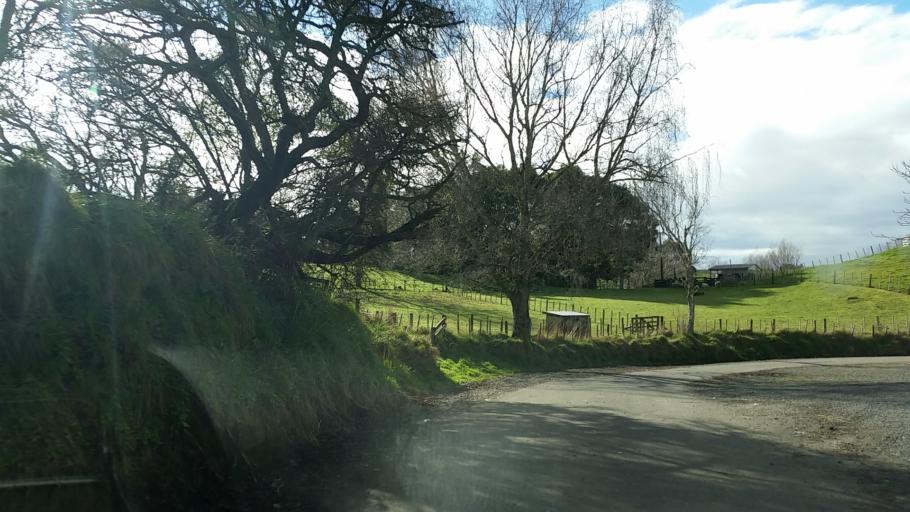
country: NZ
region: Taranaki
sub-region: South Taranaki District
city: Eltham
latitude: -39.2524
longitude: 174.5081
